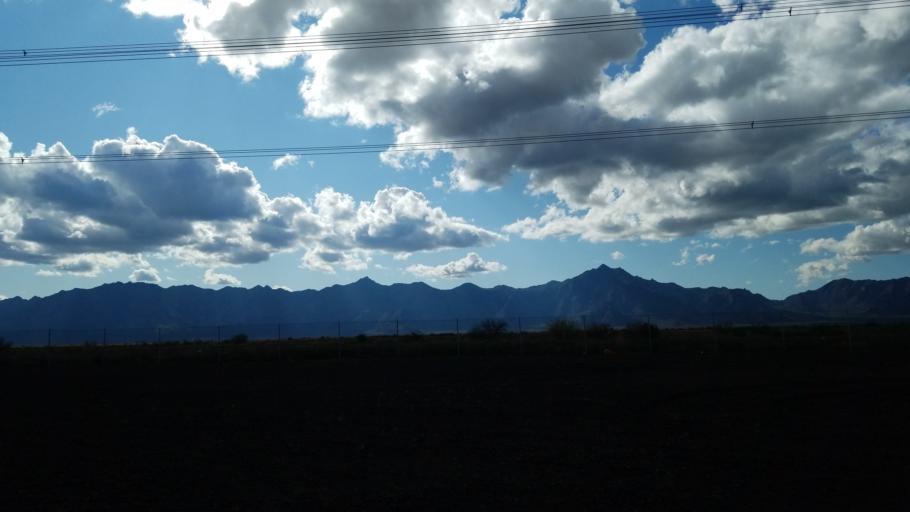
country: US
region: Arizona
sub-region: Maricopa County
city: Laveen
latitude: 33.3331
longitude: -112.1765
